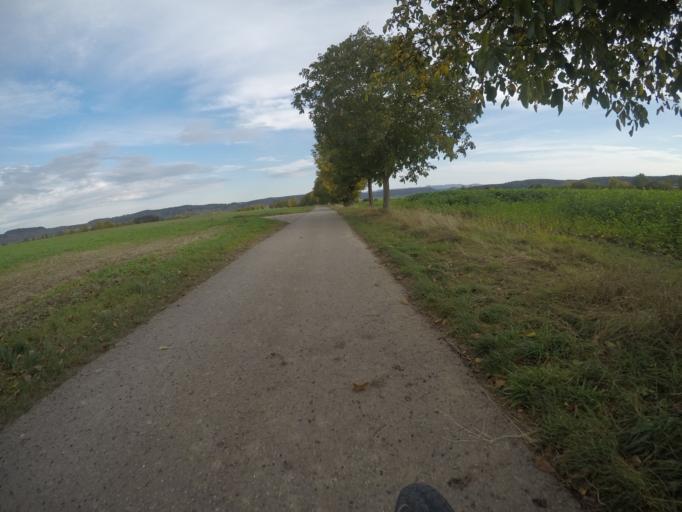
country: DE
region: Baden-Wuerttemberg
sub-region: Tuebingen Region
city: Rottenburg
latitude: 48.5425
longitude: 8.9292
